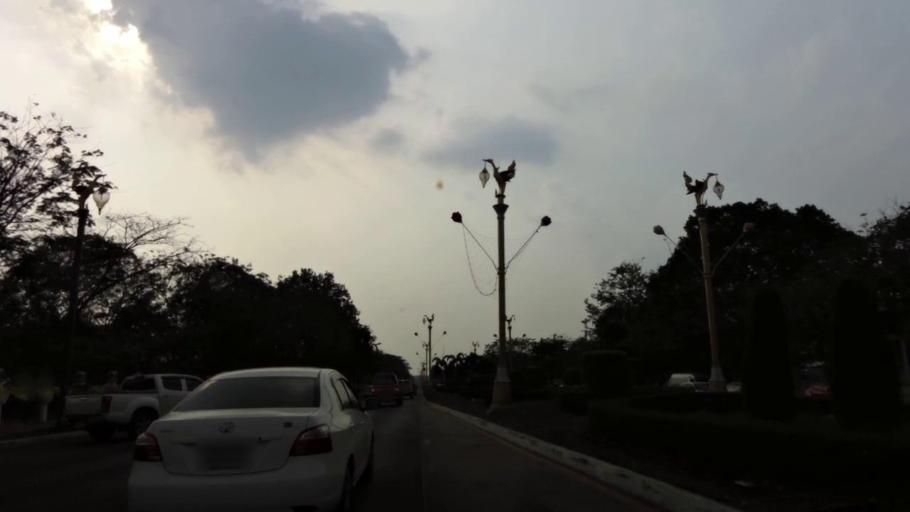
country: TH
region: Phra Nakhon Si Ayutthaya
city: Phra Nakhon Si Ayutthaya
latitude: 14.3501
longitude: 100.5682
